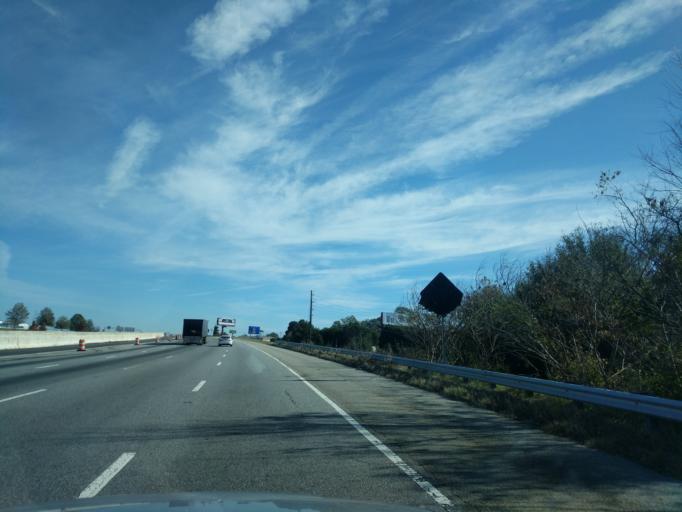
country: US
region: South Carolina
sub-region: Spartanburg County
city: Valley Falls
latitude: 35.0109
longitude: -81.9127
